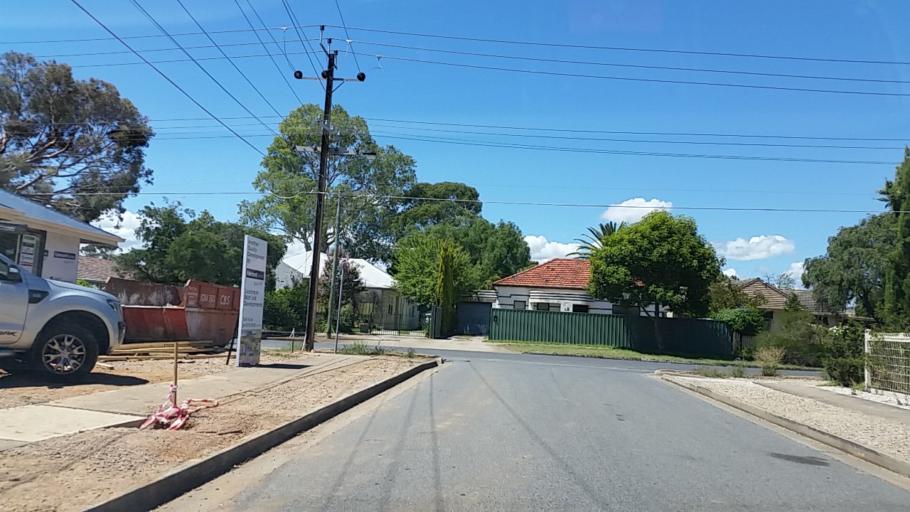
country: AU
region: South Australia
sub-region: Marion
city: South Plympton
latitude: -34.9656
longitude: 138.5652
